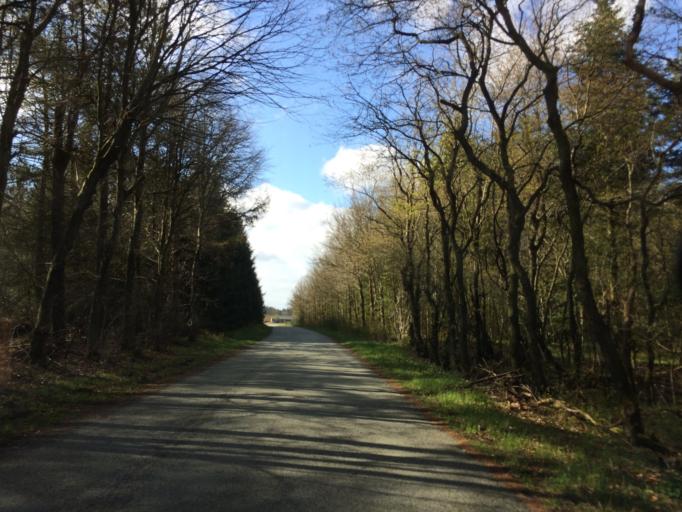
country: DK
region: Central Jutland
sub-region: Holstebro Kommune
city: Ulfborg
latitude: 56.2042
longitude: 8.4504
